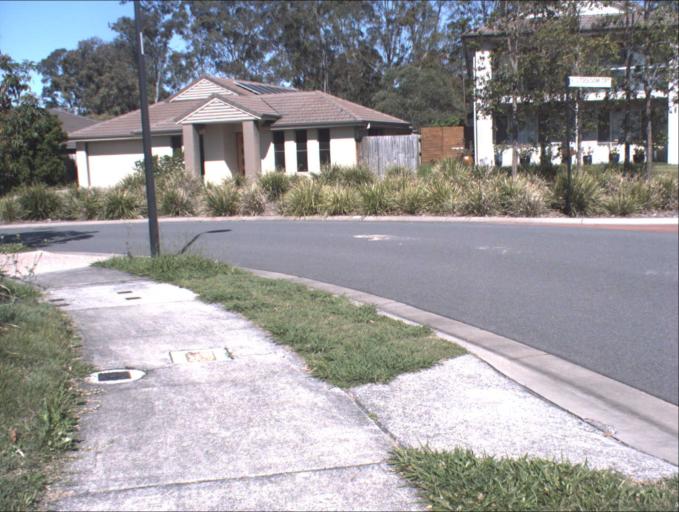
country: AU
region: Queensland
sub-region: Logan
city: Waterford West
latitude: -27.7175
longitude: 153.1429
